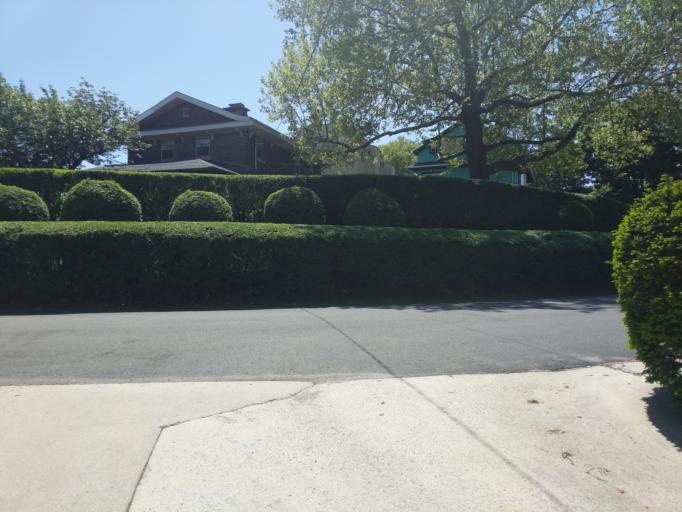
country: US
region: New Jersey
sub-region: Hudson County
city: Bayonne
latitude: 40.6374
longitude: -74.0789
